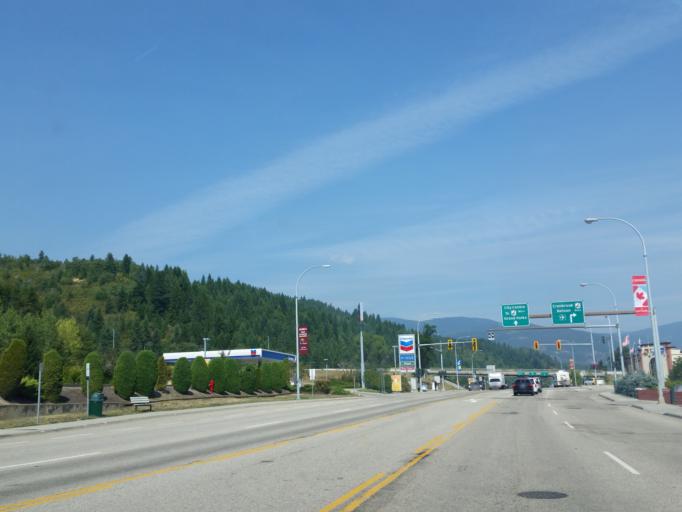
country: CA
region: British Columbia
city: Castlegar
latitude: 49.2965
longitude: -117.6544
